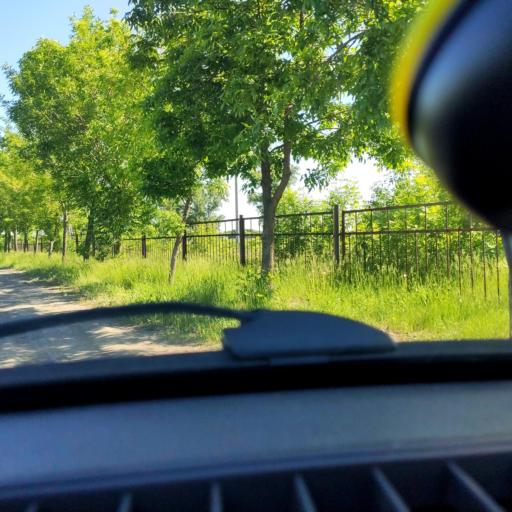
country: RU
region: Samara
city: Tol'yatti
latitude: 53.5722
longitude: 49.4302
